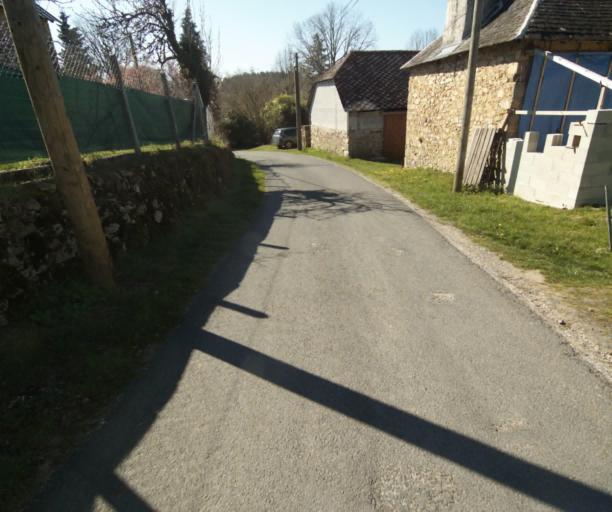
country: FR
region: Limousin
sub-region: Departement de la Correze
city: Saint-Mexant
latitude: 45.3104
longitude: 1.6224
